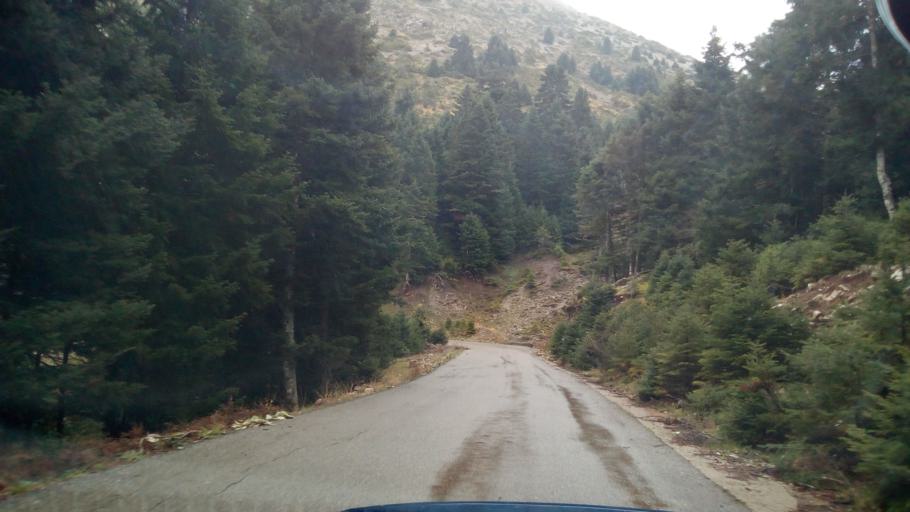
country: GR
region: West Greece
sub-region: Nomos Aitolias kai Akarnanias
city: Nafpaktos
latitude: 38.5327
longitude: 21.8506
